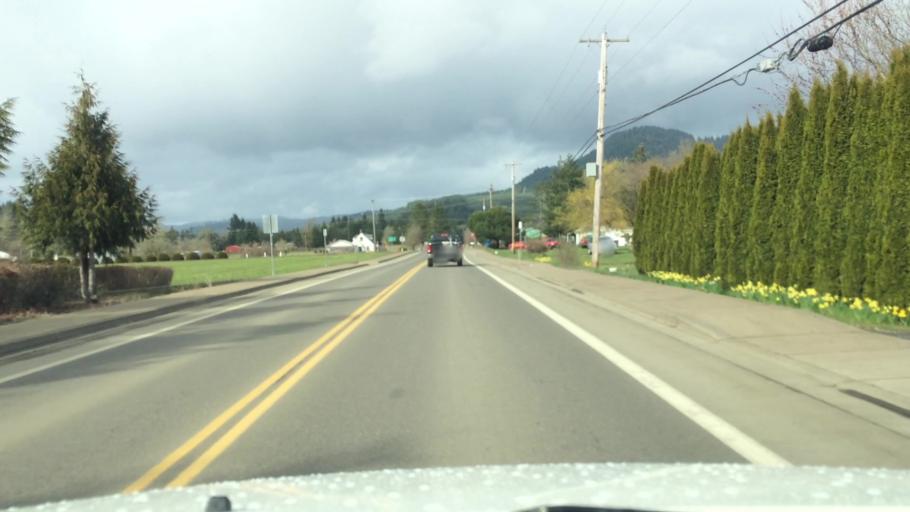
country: US
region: Oregon
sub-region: Polk County
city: Grand Ronde
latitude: 45.0784
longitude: -123.6119
